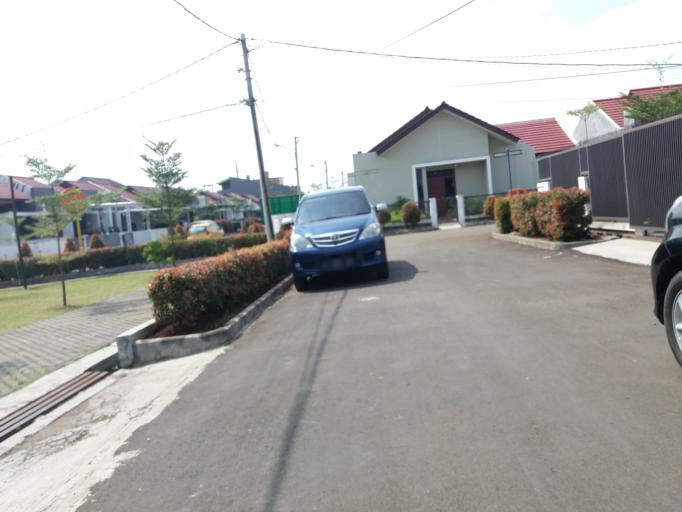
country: ID
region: West Java
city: Bandung
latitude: -6.9241
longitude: 107.6662
